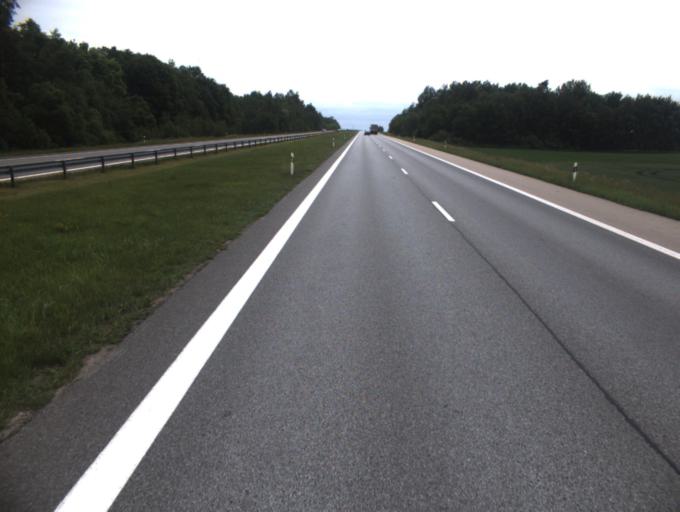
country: LT
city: Raseiniai
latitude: 55.3023
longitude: 23.2610
